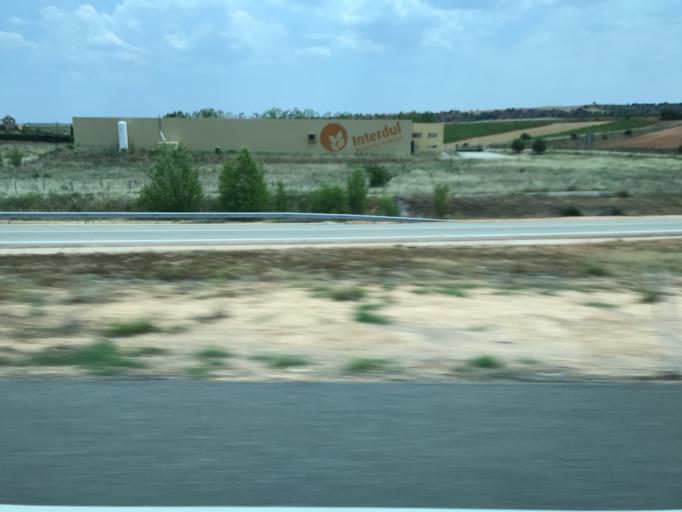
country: ES
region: Castille and Leon
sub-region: Provincia de Burgos
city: Pardilla
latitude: 41.5505
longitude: -3.7175
